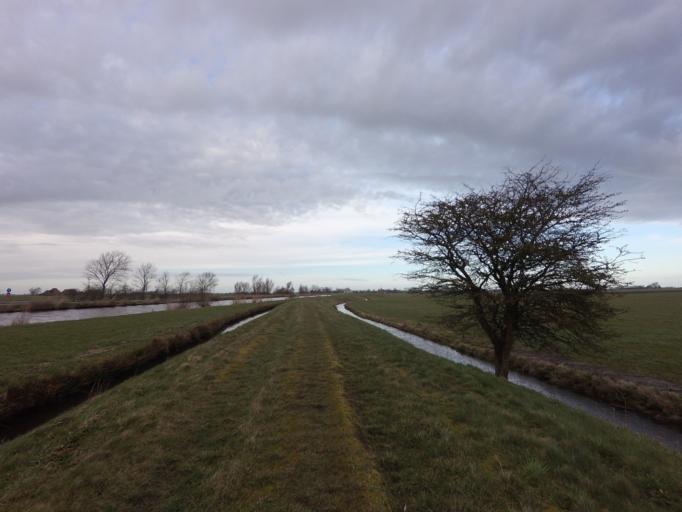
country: NL
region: Friesland
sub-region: Sudwest Fryslan
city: Bolsward
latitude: 53.0315
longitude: 5.4900
